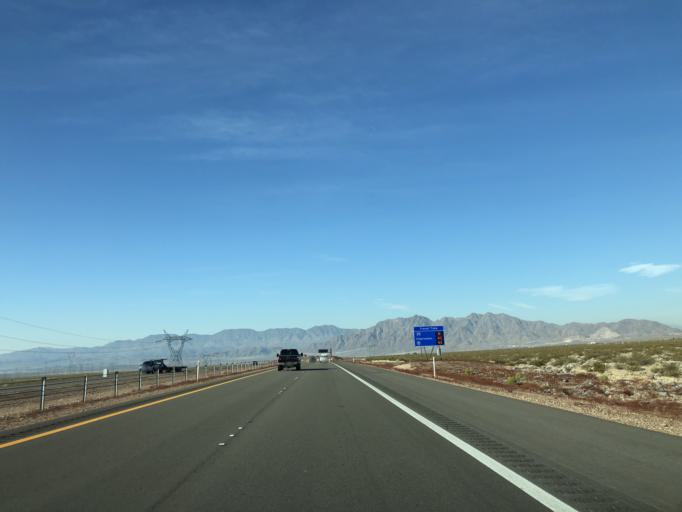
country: US
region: Nevada
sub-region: Clark County
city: Boulder City
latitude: 35.9346
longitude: -114.8324
